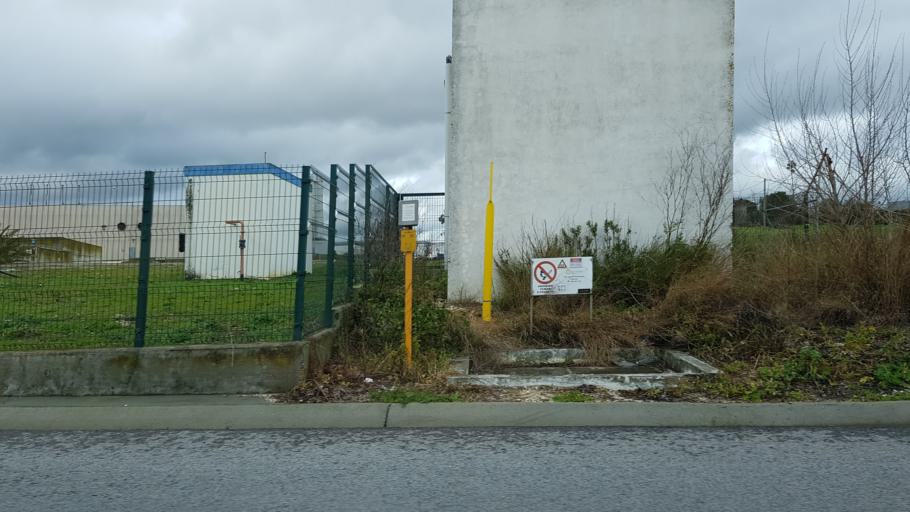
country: PT
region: Lisbon
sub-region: Alenquer
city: Carregado
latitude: 39.0319
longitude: -8.9727
